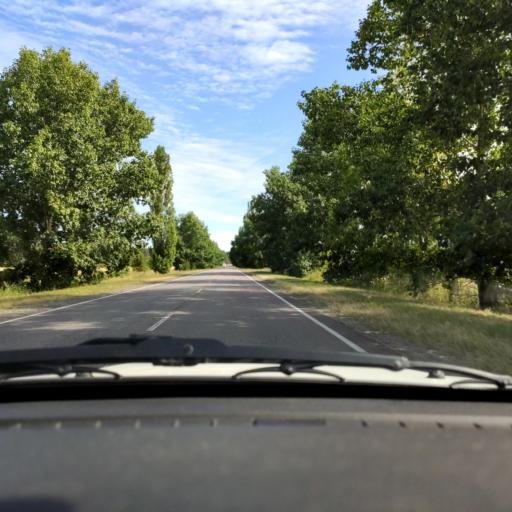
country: RU
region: Voronezj
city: Uglyanets
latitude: 51.8441
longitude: 39.6559
